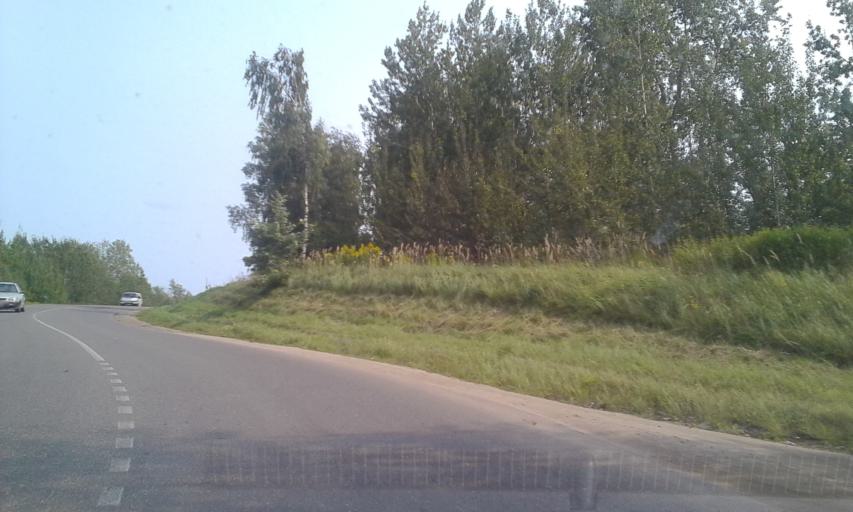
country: BY
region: Minsk
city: Hatava
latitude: 53.7699
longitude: 27.6526
